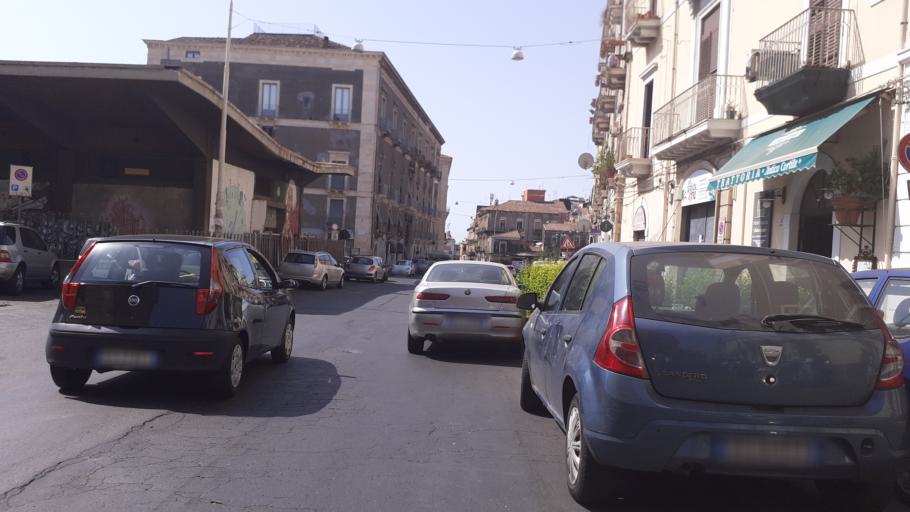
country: IT
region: Sicily
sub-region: Catania
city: Catania
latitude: 37.5046
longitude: 15.0934
